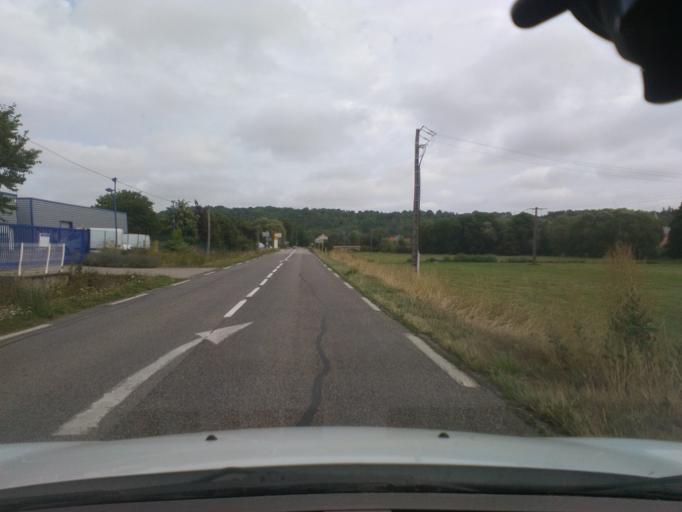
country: FR
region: Lorraine
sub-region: Departement de Meurthe-et-Moselle
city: Pulligny
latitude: 48.5209
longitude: 6.1574
